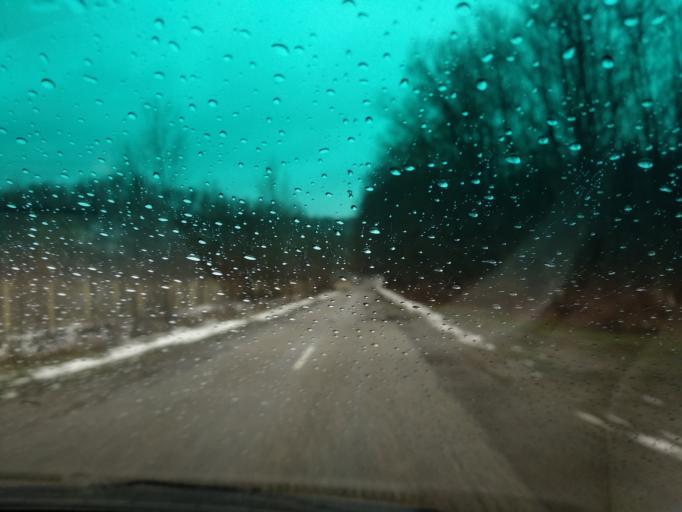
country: RU
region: Krasnodarskiy
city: Khadyzhensk
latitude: 44.2205
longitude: 39.3927
